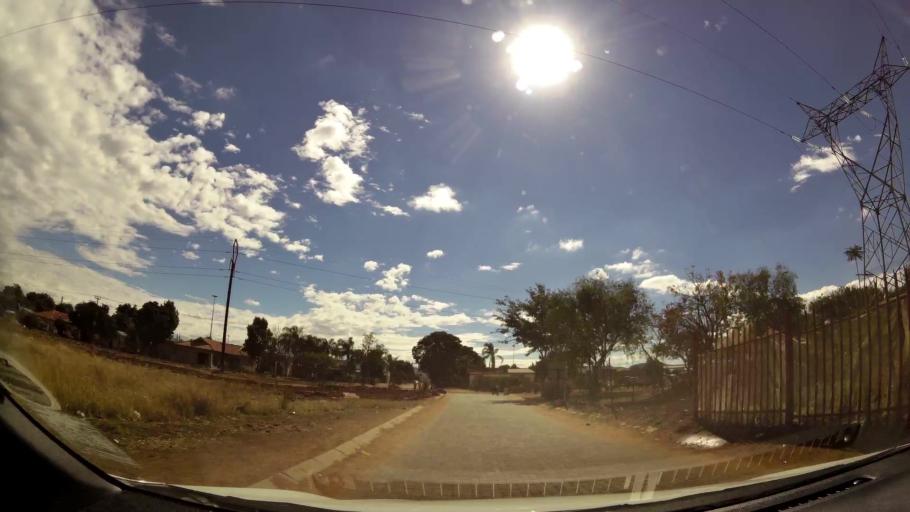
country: ZA
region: Limpopo
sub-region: Waterberg District Municipality
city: Bela-Bela
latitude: -24.8909
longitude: 28.3204
